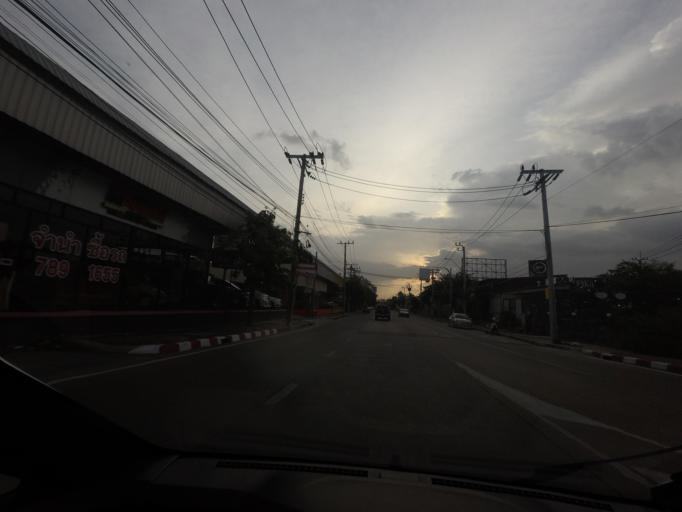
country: TH
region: Bangkok
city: Lat Phrao
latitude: 13.8203
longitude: 100.6336
